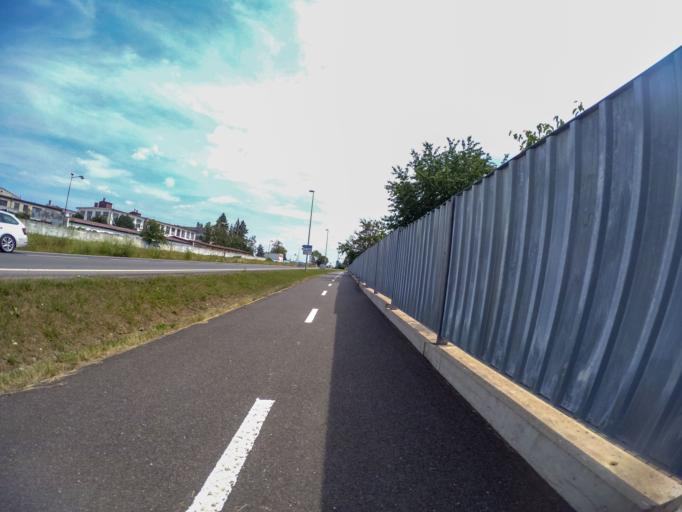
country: CZ
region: Praha
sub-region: Praha 19
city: Kbely
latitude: 50.1297
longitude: 14.5401
